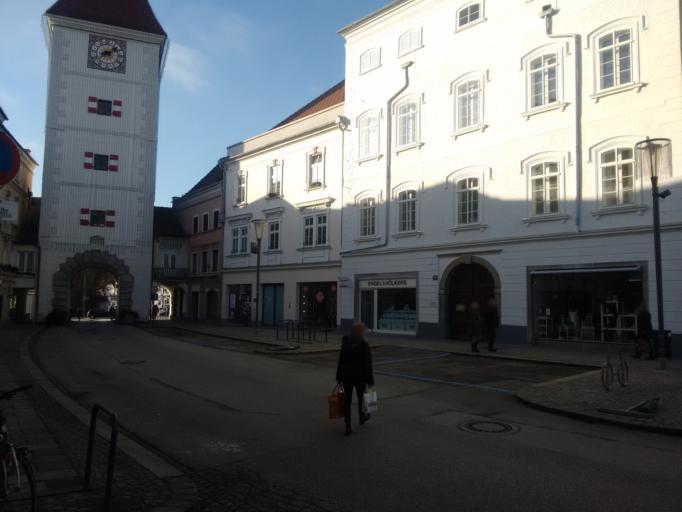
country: AT
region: Upper Austria
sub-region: Wels-Land
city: Thalheim bei Wels
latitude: 48.1580
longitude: 14.0251
